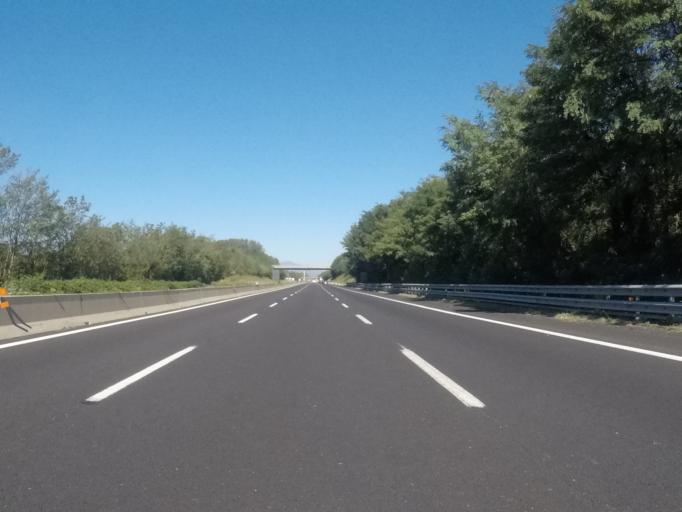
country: IT
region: Campania
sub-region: Provincia di Caserta
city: Caianello
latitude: 41.3243
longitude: 14.0797
